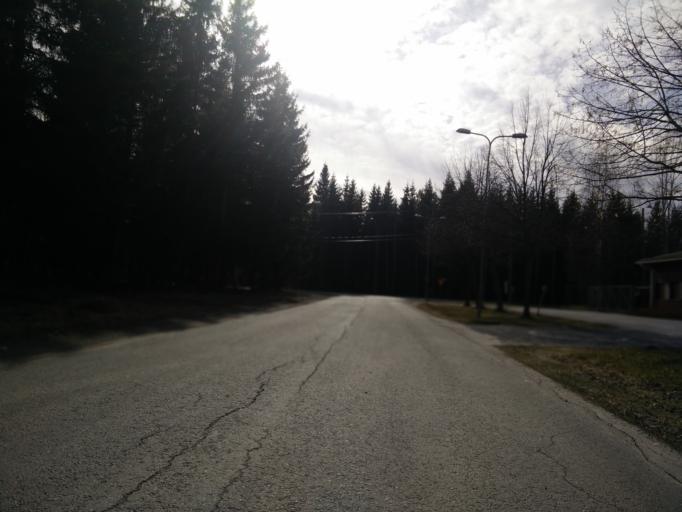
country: FI
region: Pirkanmaa
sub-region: Tampere
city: Orivesi
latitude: 61.6922
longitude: 24.3650
